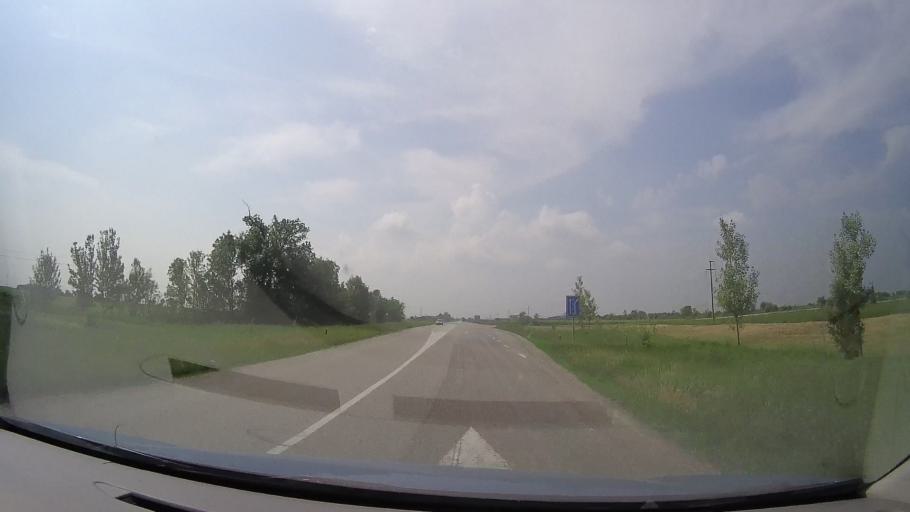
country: RS
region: Autonomna Pokrajina Vojvodina
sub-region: Juznobanatski Okrug
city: Kovacica
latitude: 45.0783
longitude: 20.6411
